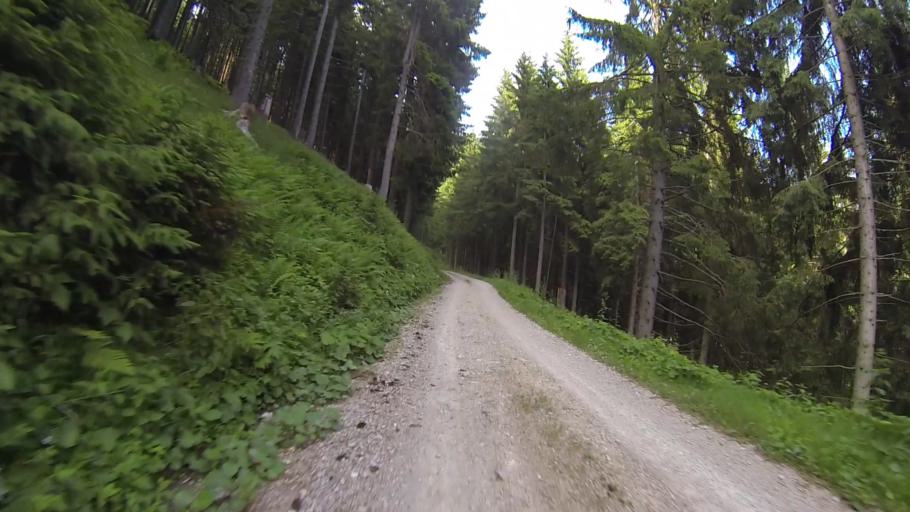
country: DE
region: Bavaria
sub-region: Swabia
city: Nesselwang
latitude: 47.5849
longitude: 10.4952
